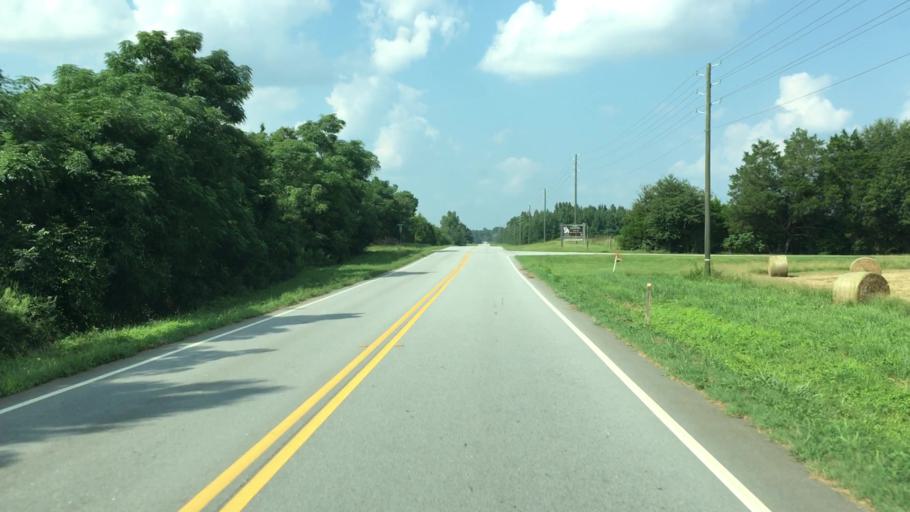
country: US
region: Georgia
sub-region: Jasper County
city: Monticello
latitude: 33.4415
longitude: -83.7579
